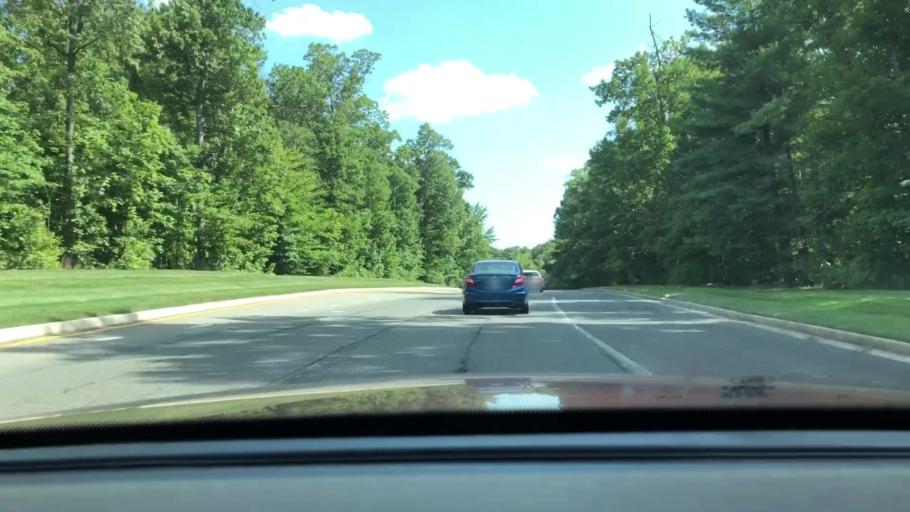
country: US
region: Virginia
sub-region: Fairfax County
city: Chantilly
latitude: 38.8759
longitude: -77.4553
